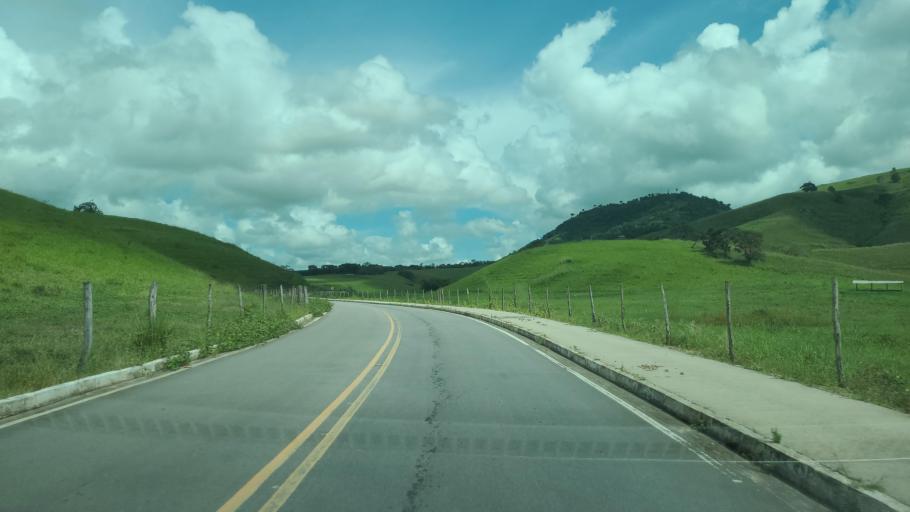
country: BR
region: Alagoas
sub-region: Uniao Dos Palmares
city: Uniao dos Palmares
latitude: -9.1636
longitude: -36.0541
